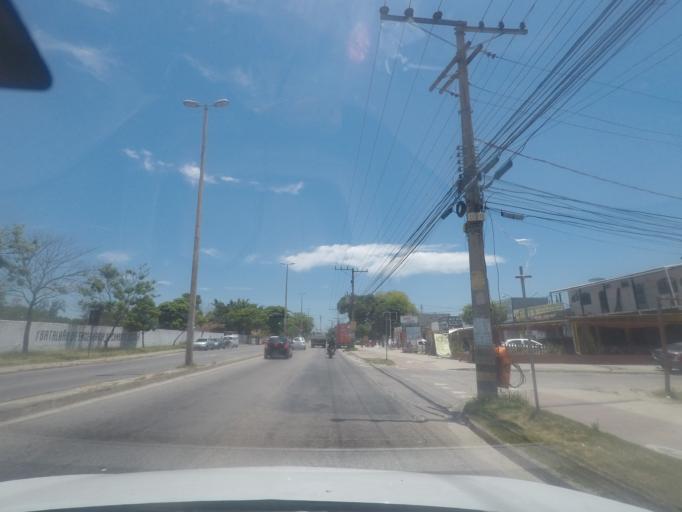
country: BR
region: Rio de Janeiro
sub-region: Itaguai
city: Itaguai
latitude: -22.9079
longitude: -43.6858
